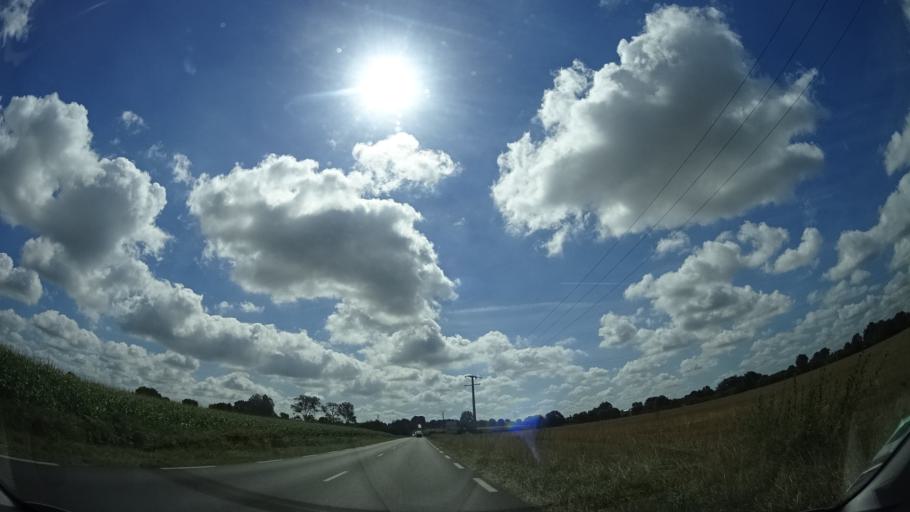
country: FR
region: Pays de la Loire
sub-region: Departement de la Mayenne
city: Meslay-du-Maine
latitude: 47.9627
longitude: -0.5764
